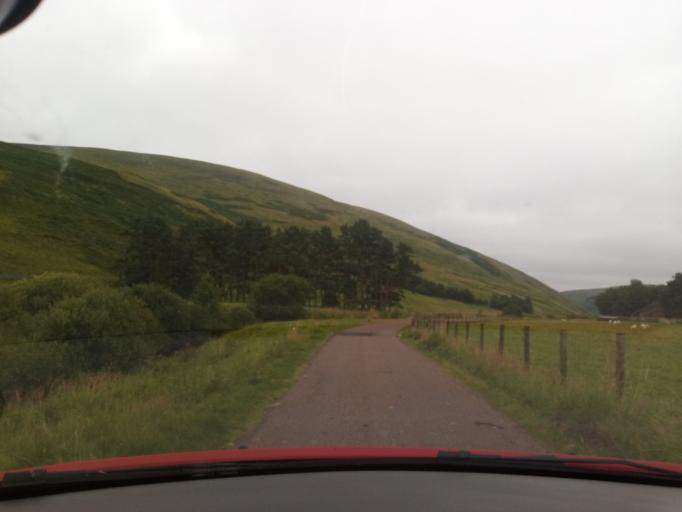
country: GB
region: England
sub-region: Northumberland
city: Rochester
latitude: 55.3886
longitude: -2.2118
